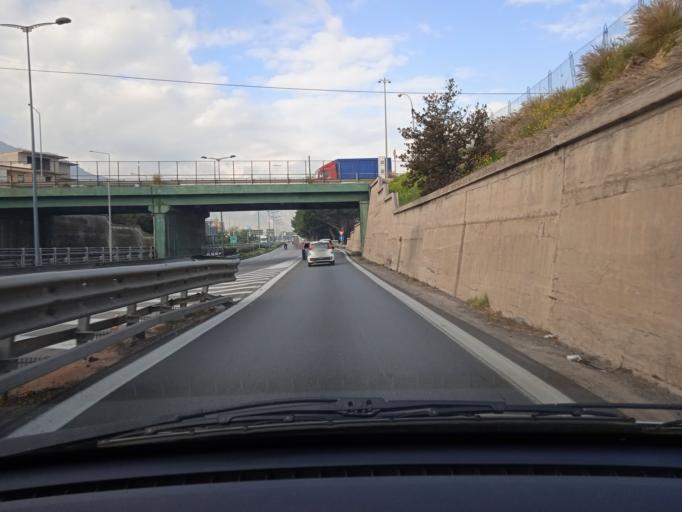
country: IT
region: Sicily
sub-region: Palermo
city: Villabate
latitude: 38.0862
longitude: 13.4341
